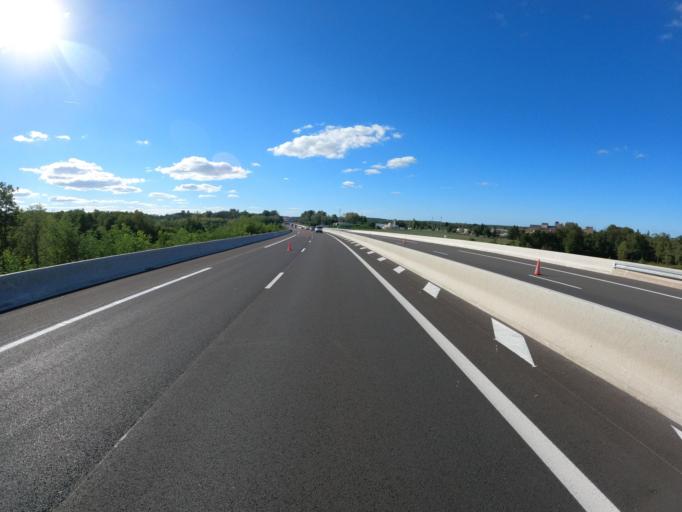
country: FR
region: Auvergne
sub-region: Departement de l'Allier
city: Dompierre-sur-Besbre
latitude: 46.5354
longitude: 3.7072
